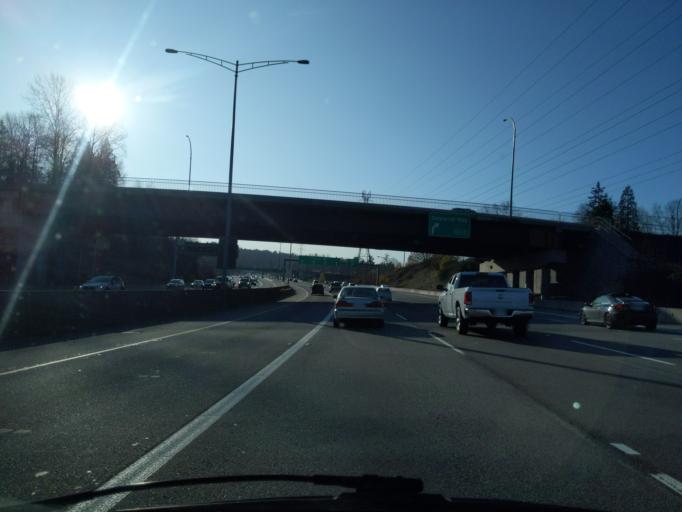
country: CA
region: British Columbia
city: New Westminster
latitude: 49.2469
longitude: -122.9104
